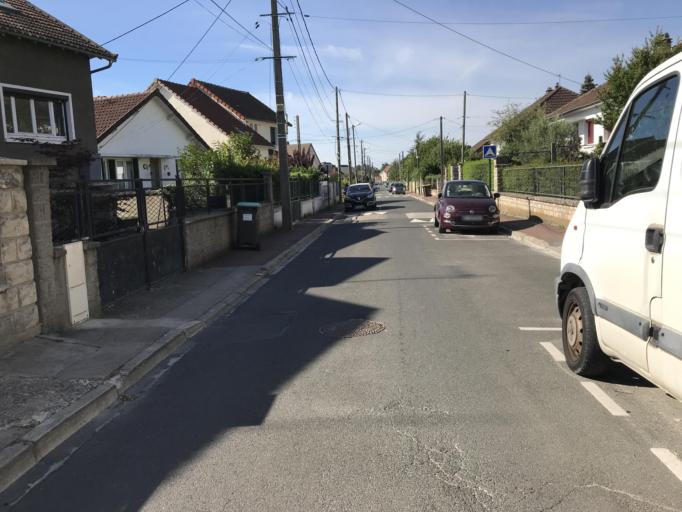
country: FR
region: Ile-de-France
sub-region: Departement de l'Essonne
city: Saint-Michel-sur-Orge
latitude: 48.6387
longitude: 2.3053
